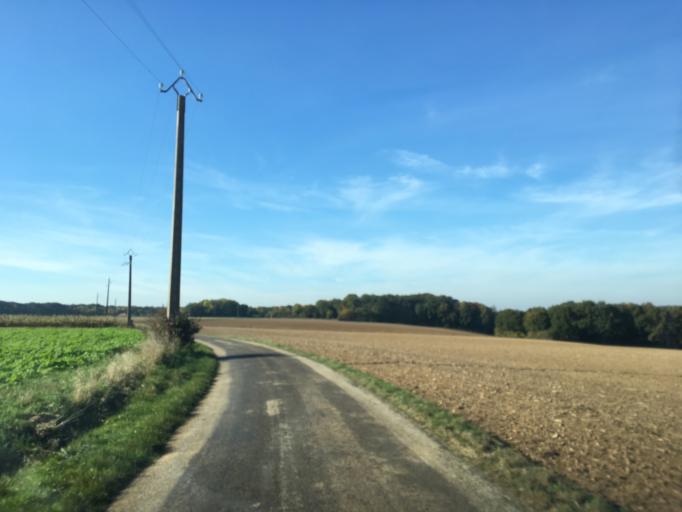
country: FR
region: Haute-Normandie
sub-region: Departement de l'Eure
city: Heudreville-sur-Eure
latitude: 49.1421
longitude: 1.2263
